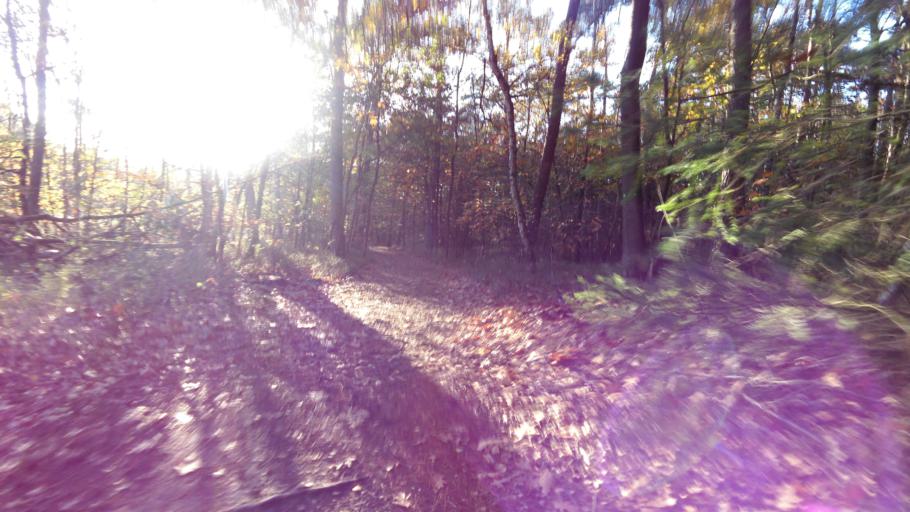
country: NL
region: Gelderland
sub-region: Gemeente Epe
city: Epe
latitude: 52.3729
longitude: 5.9827
